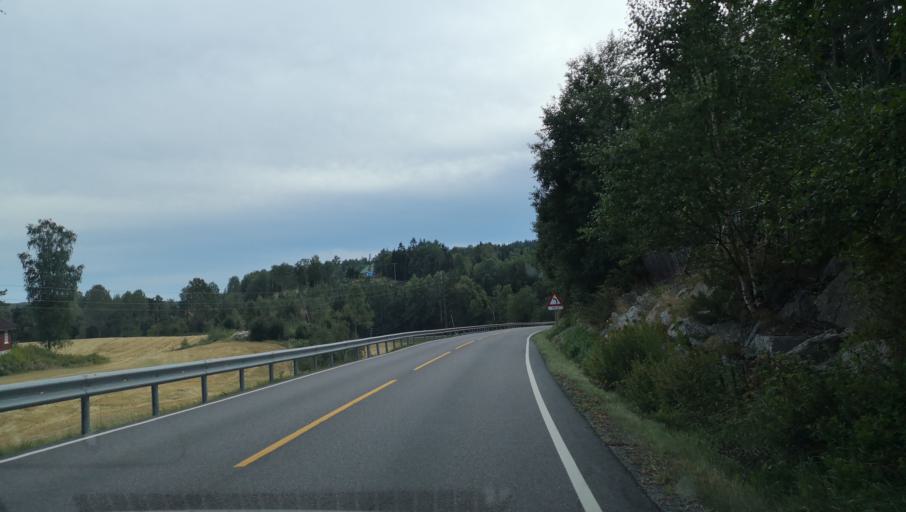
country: NO
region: Ostfold
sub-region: Hobol
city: Tomter
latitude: 59.7124
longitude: 11.0510
